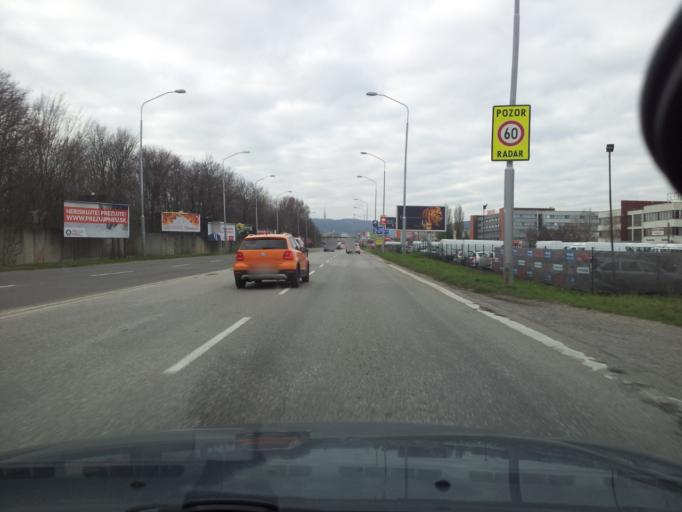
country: SK
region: Bratislavsky
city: Svaty Jur
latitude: 48.1895
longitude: 17.1896
